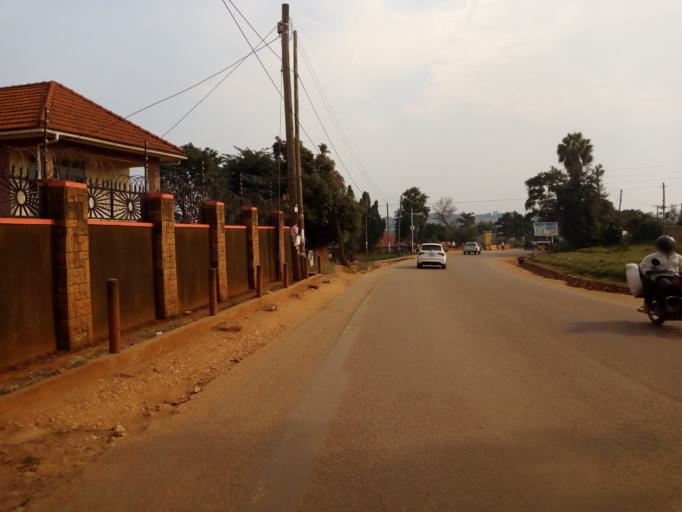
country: UG
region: Central Region
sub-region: Wakiso District
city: Kireka
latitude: 0.3195
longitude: 32.6335
